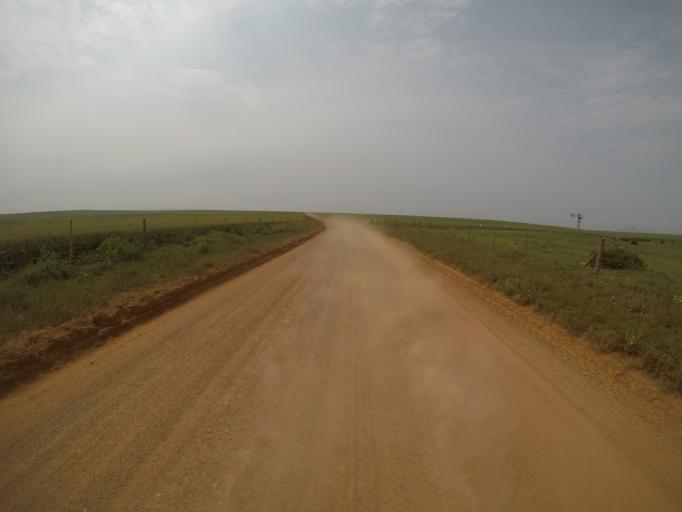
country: ZA
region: Western Cape
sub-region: City of Cape Town
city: Kraaifontein
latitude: -33.7236
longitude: 18.6692
